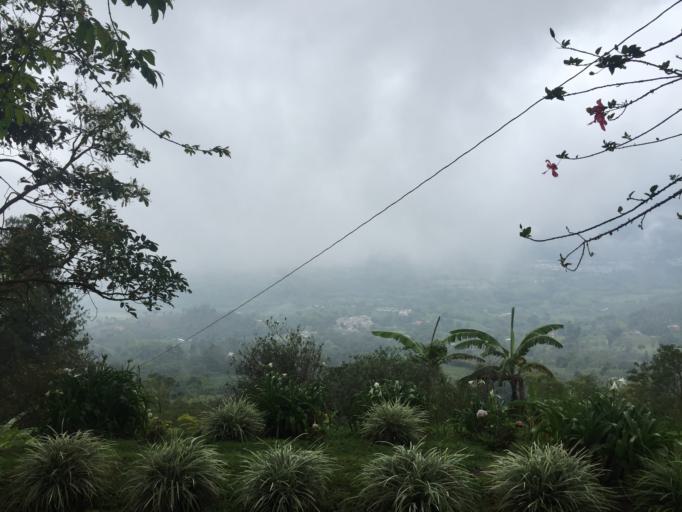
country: CO
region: Quindio
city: Calarca
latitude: 4.4821
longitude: -75.6345
